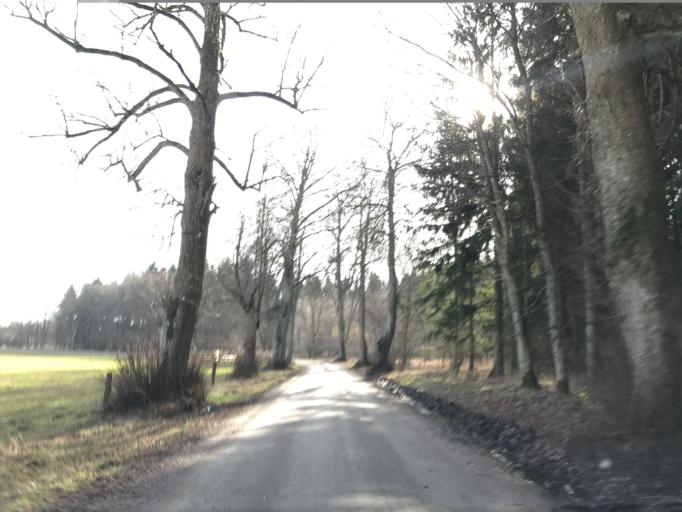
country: SE
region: Skane
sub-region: Tomelilla Kommun
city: Tomelilla
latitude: 55.5204
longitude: 13.8915
